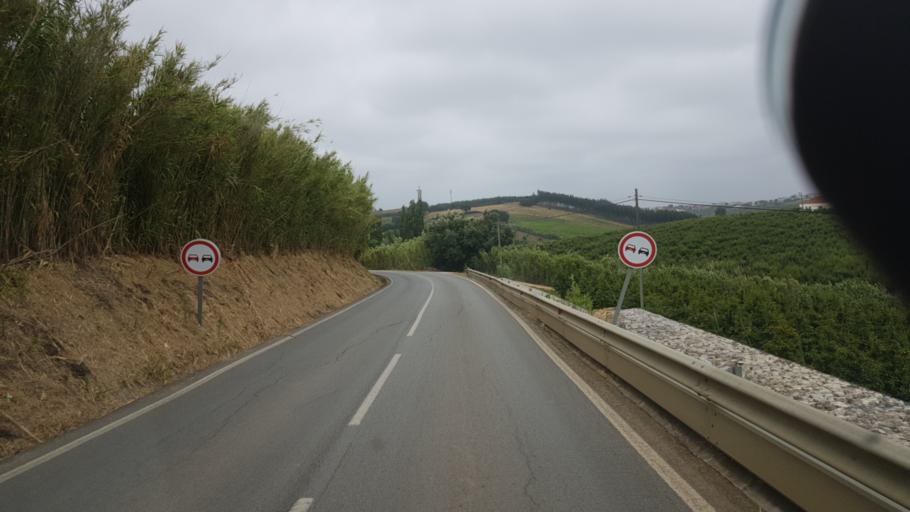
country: PT
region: Leiria
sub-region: Bombarral
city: Bombarral
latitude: 39.2740
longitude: -9.1726
